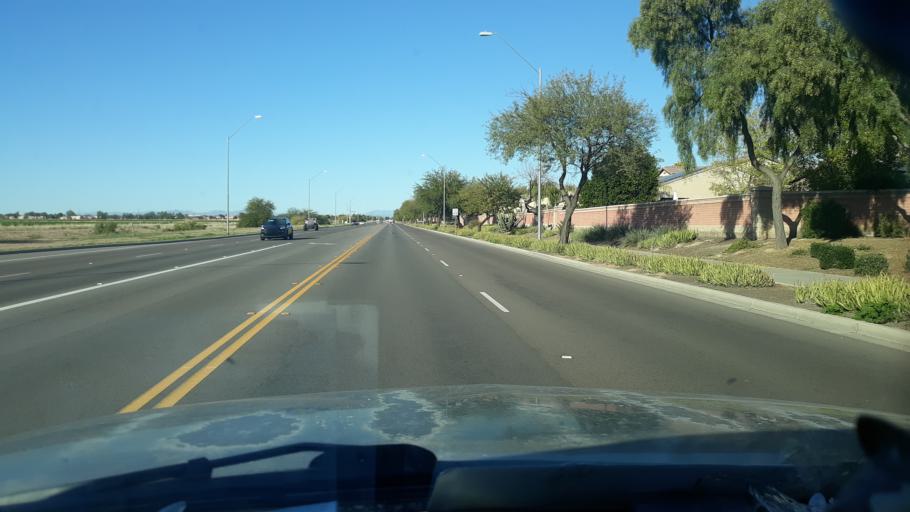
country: US
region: Arizona
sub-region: Maricopa County
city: Surprise
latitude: 33.5988
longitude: -112.3938
